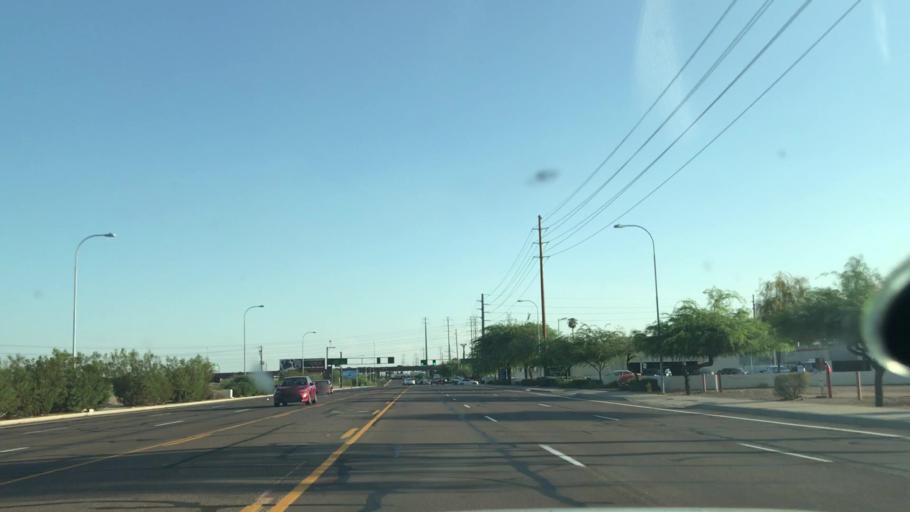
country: US
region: Arizona
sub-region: Maricopa County
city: Tempe
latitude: 33.4422
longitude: -111.9095
